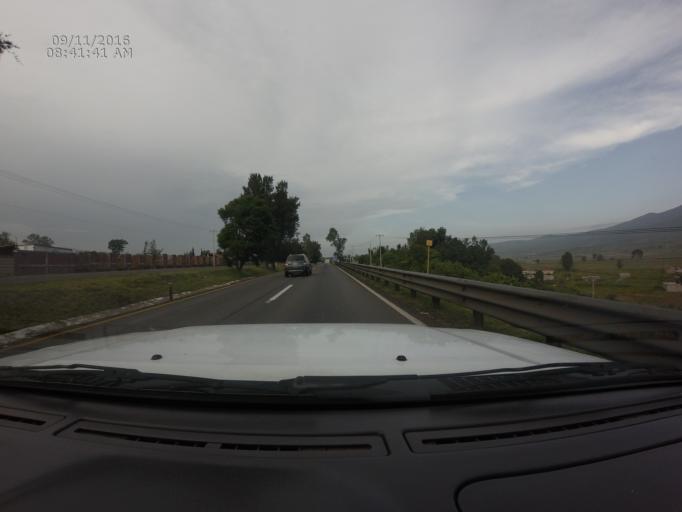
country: MX
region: Michoacan
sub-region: Morelia
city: La Mintzita (Piedra Dura)
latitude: 19.5970
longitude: -101.2936
